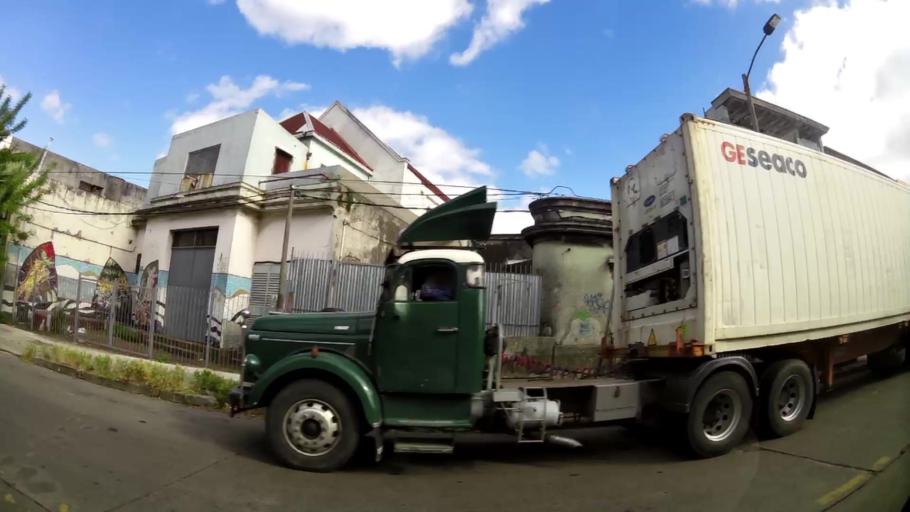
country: UY
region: Montevideo
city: Montevideo
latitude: -34.8856
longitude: -56.1754
